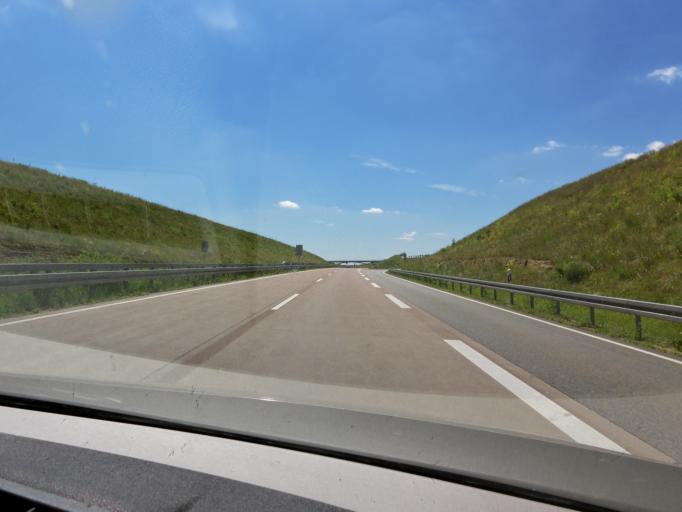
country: DE
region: Thuringia
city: Bretleben
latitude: 51.3279
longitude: 11.2490
